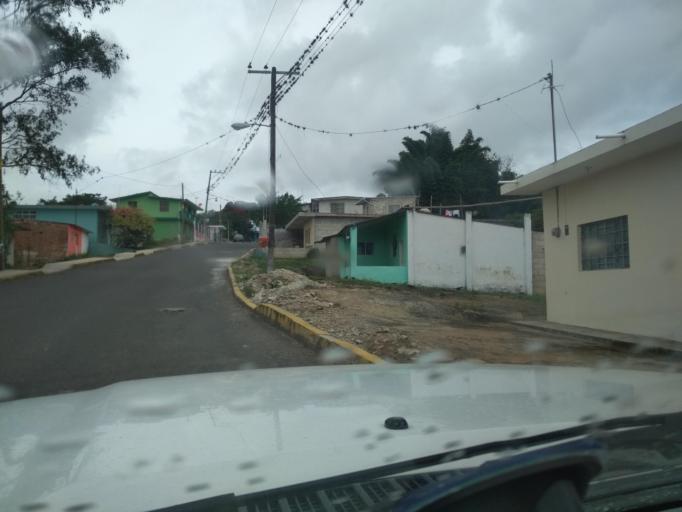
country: MX
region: Veracruz
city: El Castillo
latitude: 19.5344
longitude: -96.8151
